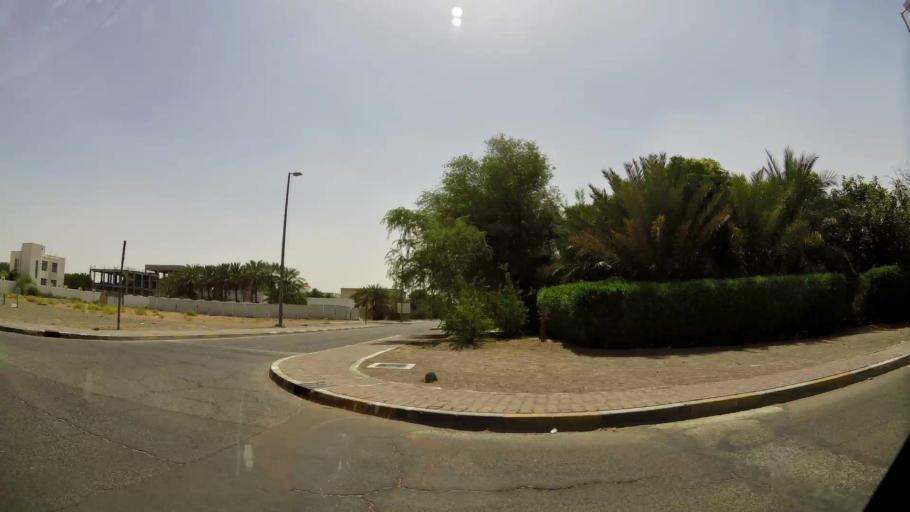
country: AE
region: Abu Dhabi
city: Al Ain
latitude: 24.2374
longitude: 55.7125
